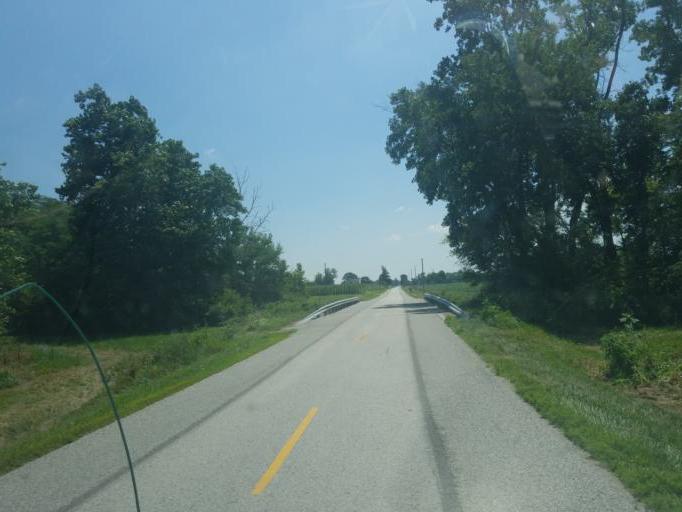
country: US
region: Ohio
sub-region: Auglaize County
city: Saint Marys
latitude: 40.5466
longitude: -84.2974
